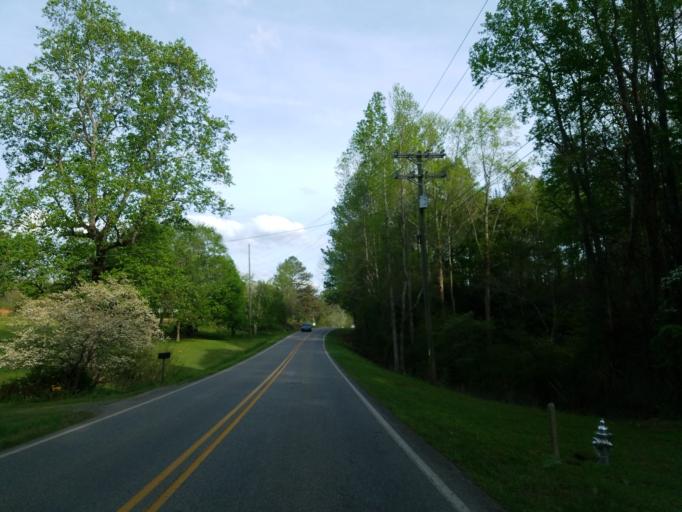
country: US
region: Georgia
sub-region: Pickens County
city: Nelson
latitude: 34.4466
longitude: -84.3449
